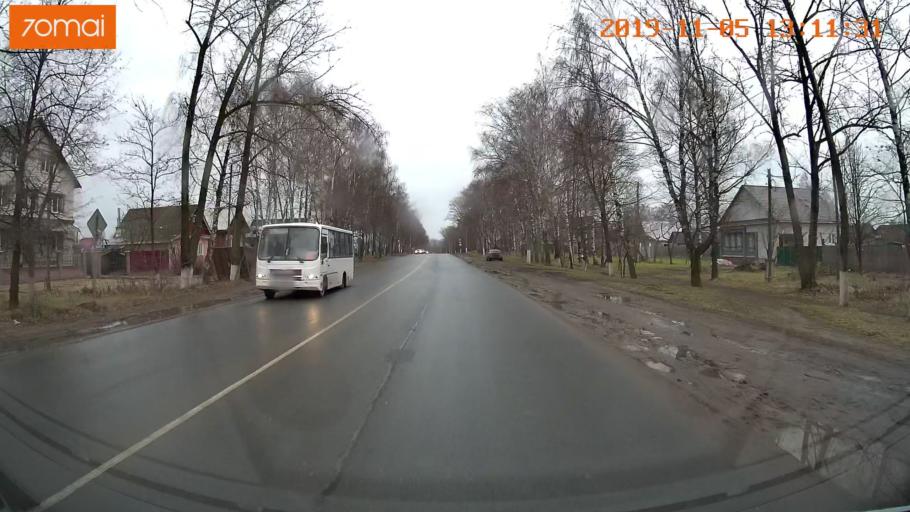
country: RU
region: Ivanovo
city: Shuya
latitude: 56.8588
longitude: 41.3403
